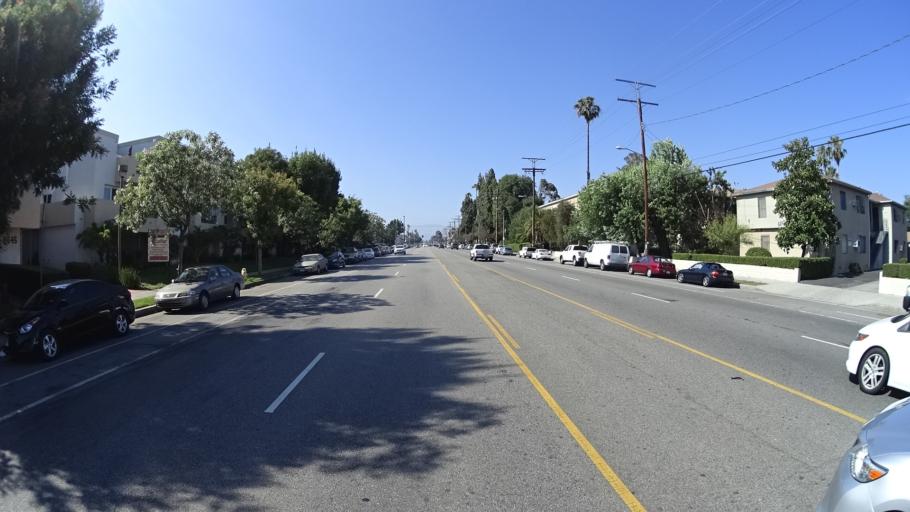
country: US
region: California
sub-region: Los Angeles County
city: Van Nuys
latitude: 34.1914
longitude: -118.4320
